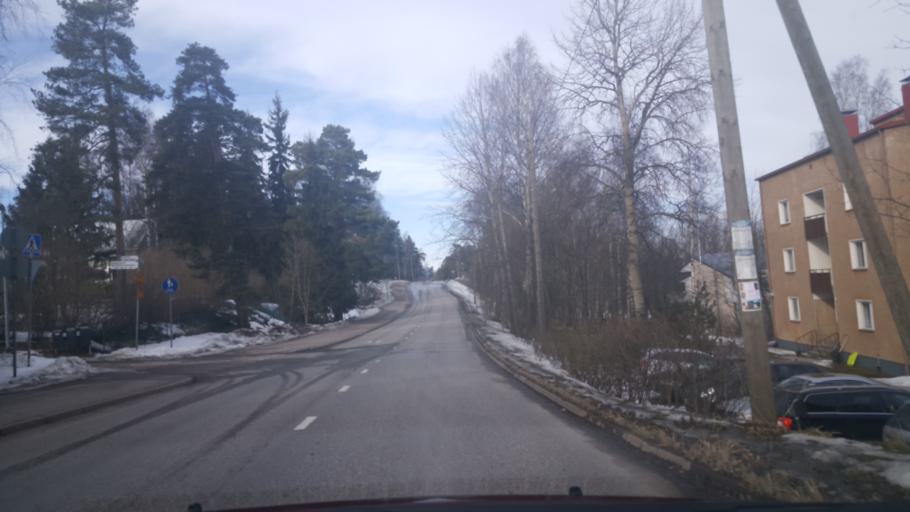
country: FI
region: Uusimaa
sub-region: Helsinki
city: Teekkarikylae
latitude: 60.2786
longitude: 24.8751
